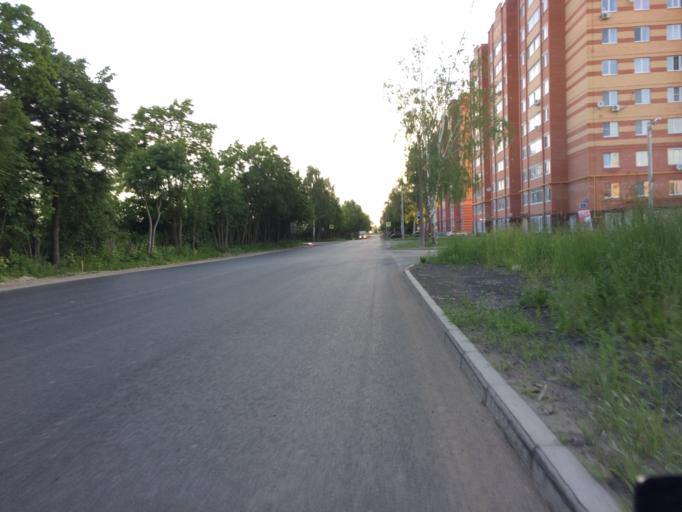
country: RU
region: Mariy-El
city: Medvedevo
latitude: 56.6440
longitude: 47.8314
